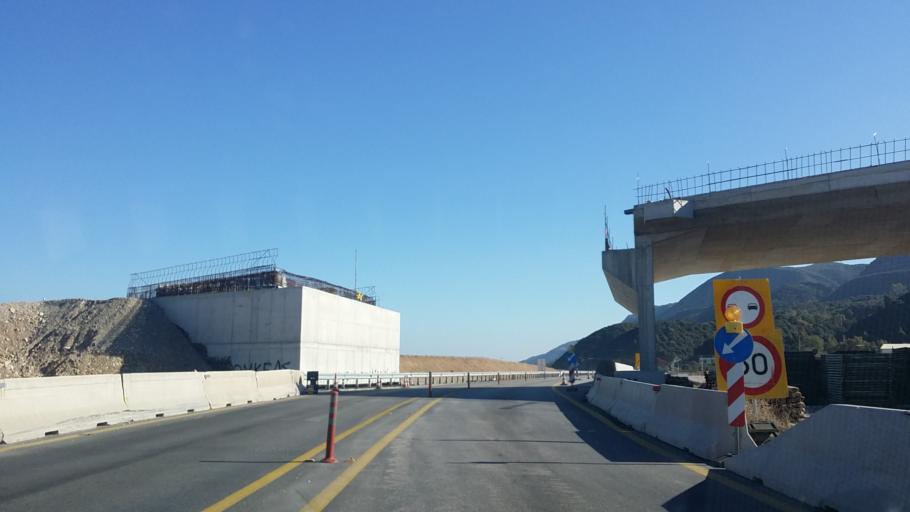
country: GR
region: West Greece
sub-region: Nomos Achaias
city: Ano Kastritsion
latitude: 38.3243
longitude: 21.8551
